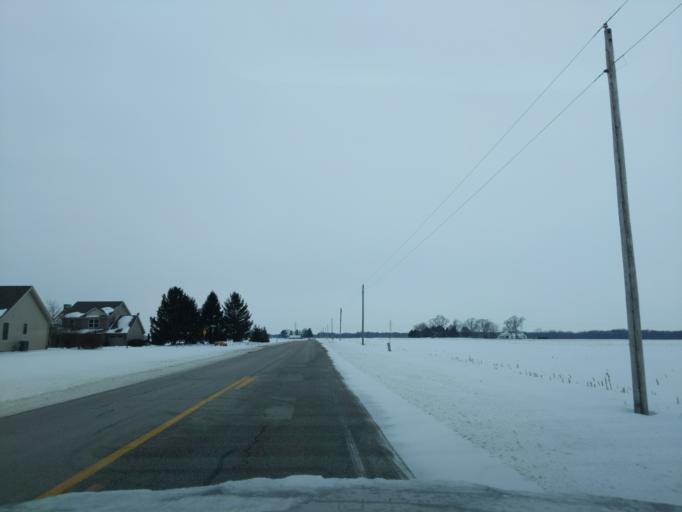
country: US
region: Indiana
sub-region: Benton County
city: Otterbein
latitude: 40.4168
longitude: -87.0716
